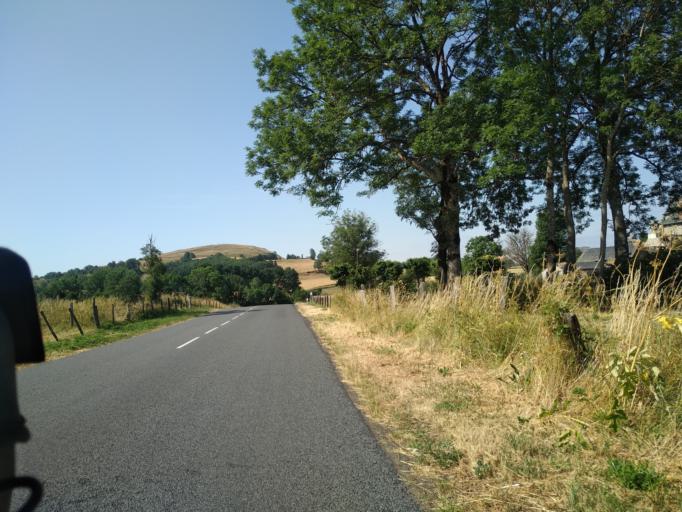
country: FR
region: Auvergne
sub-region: Departement du Cantal
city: Riom-es-Montagnes
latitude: 45.2335
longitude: 2.7334
